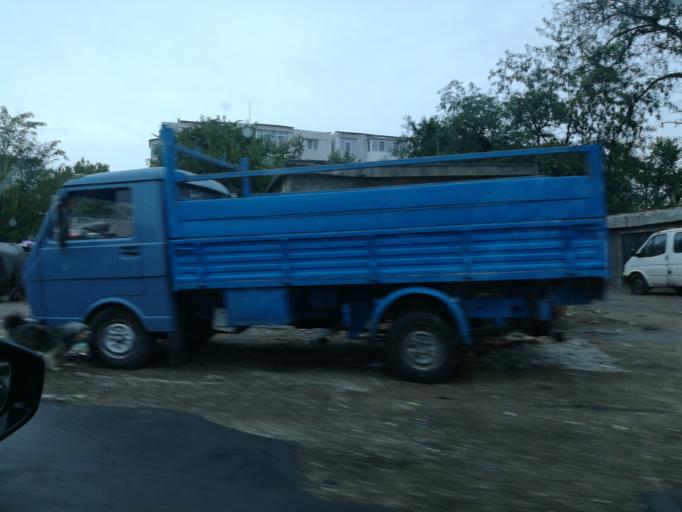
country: RO
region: Galati
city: Galati
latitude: 45.4496
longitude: 28.0152
